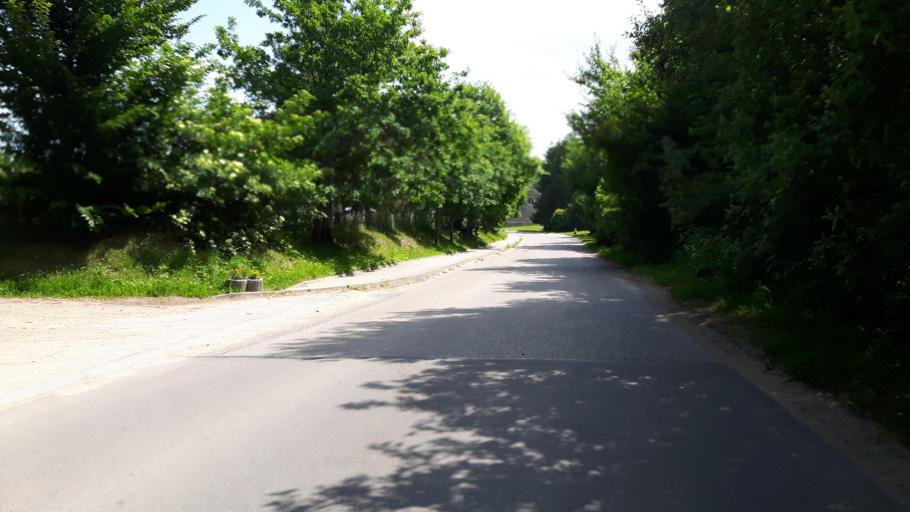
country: PL
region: Pomeranian Voivodeship
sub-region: Powiat wejherowski
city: Choczewo
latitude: 54.7566
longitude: 17.7830
